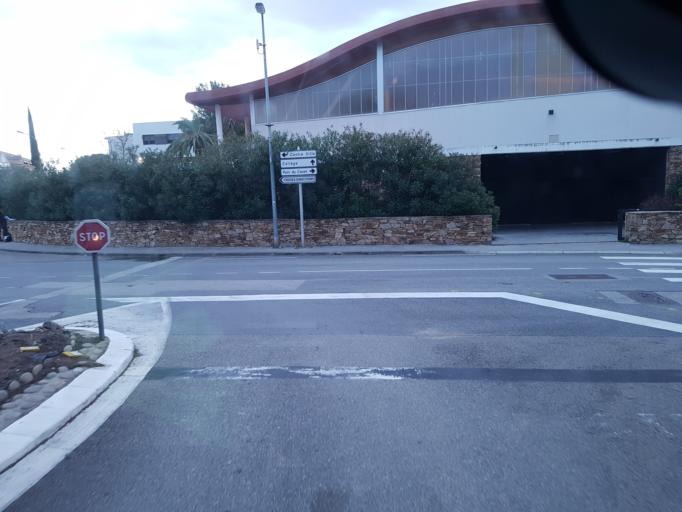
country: FR
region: Provence-Alpes-Cote d'Azur
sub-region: Departement du Var
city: Bandol
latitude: 43.1400
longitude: 5.7478
